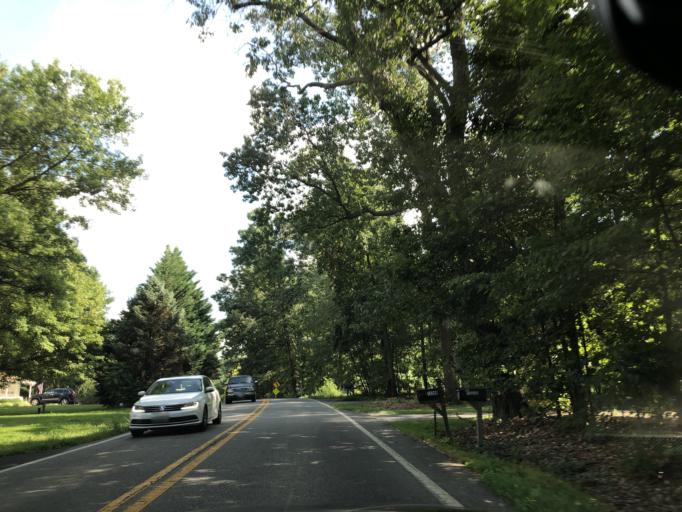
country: US
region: Maryland
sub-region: Frederick County
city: Linganore
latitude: 39.4032
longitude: -77.1983
